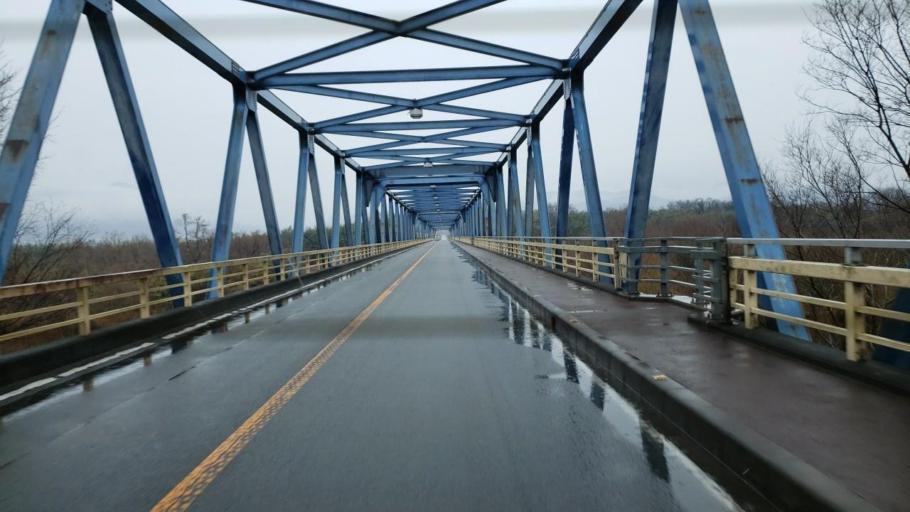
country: JP
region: Tokushima
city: Kamojimacho-jogejima
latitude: 34.0704
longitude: 134.2811
